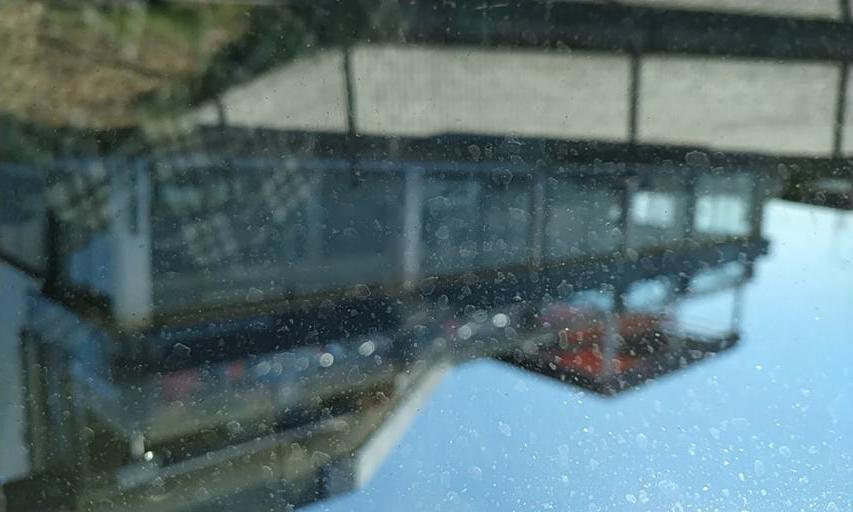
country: PT
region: Braganca
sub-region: Braganca Municipality
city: Braganca
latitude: 41.7995
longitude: -6.7698
